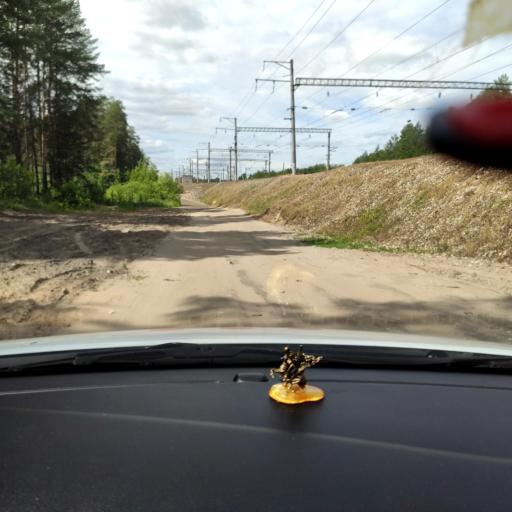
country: RU
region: Tatarstan
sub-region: Zelenodol'skiy Rayon
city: Vasil'yevo
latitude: 55.8418
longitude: 48.7270
